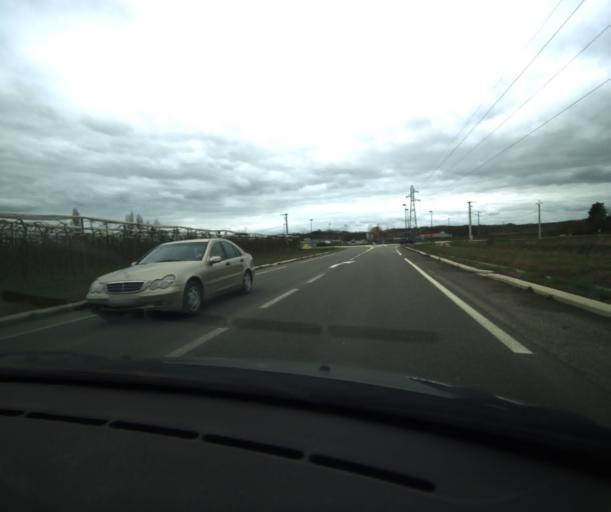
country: FR
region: Midi-Pyrenees
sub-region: Departement du Tarn-et-Garonne
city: Moissac
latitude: 44.1028
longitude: 1.1133
